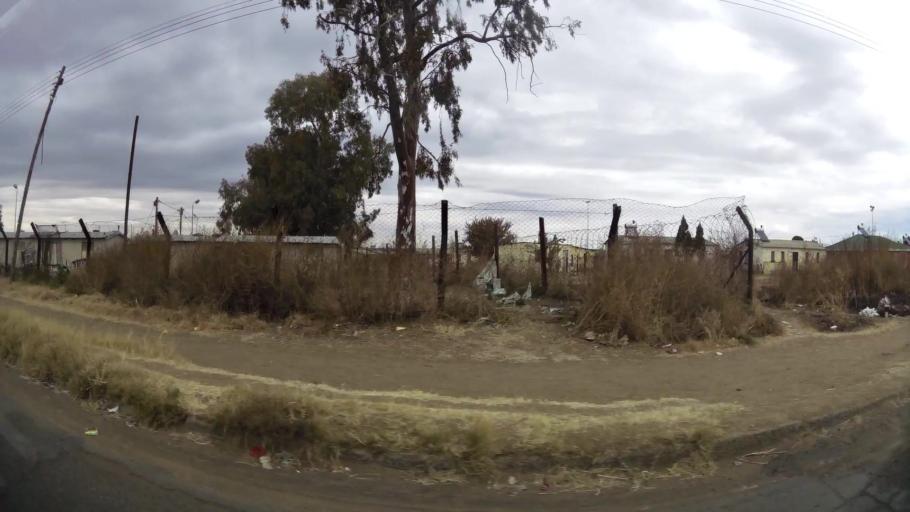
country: ZA
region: Orange Free State
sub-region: Fezile Dabi District Municipality
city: Kroonstad
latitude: -27.6525
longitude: 27.2115
